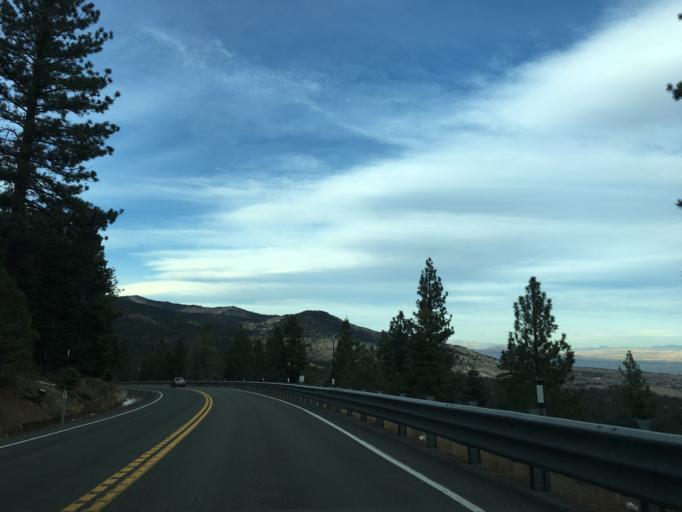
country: US
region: Nevada
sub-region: Washoe County
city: Incline Village
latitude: 39.3464
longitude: -119.8486
